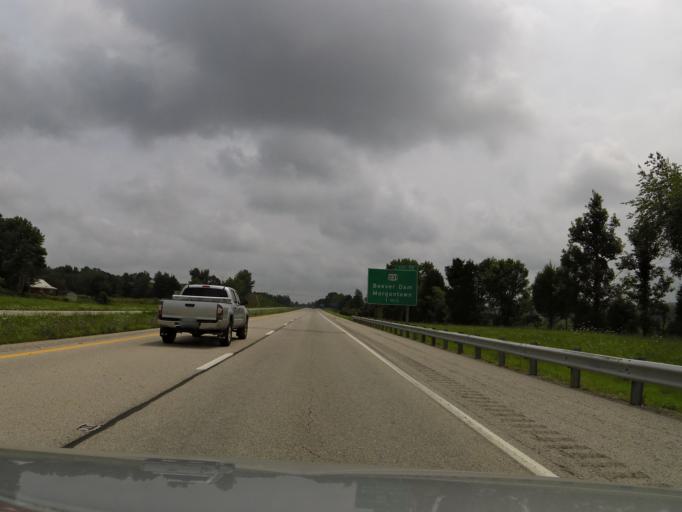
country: US
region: Kentucky
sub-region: Ohio County
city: Beaver Dam
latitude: 37.3593
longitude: -86.8652
